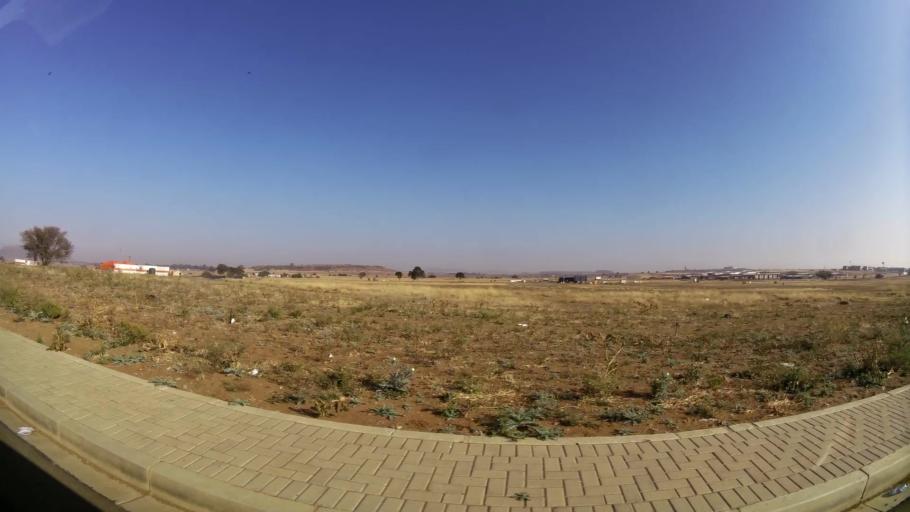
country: ZA
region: Orange Free State
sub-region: Mangaung Metropolitan Municipality
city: Bloemfontein
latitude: -29.1944
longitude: 26.2181
